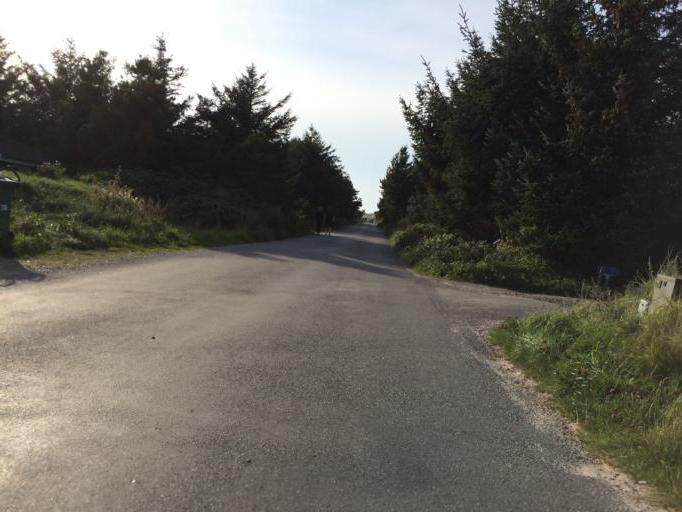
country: DK
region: Central Jutland
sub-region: Ringkobing-Skjern Kommune
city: Hvide Sande
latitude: 55.8675
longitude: 8.1747
